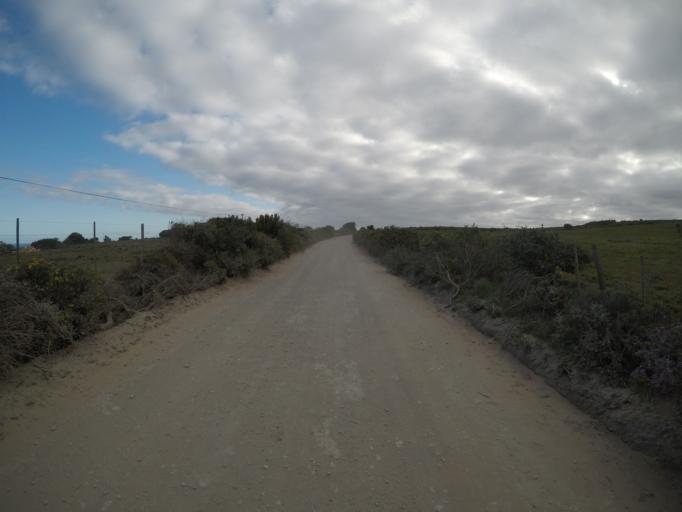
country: ZA
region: Western Cape
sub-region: Eden District Municipality
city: Riversdale
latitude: -34.4193
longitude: 21.3383
